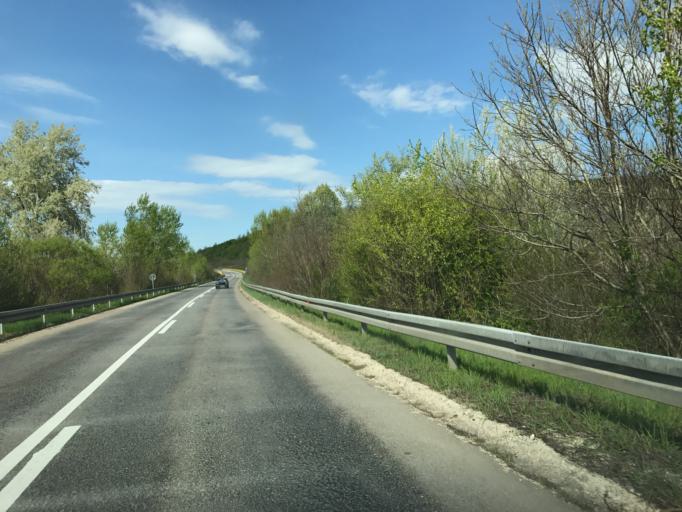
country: RS
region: Central Serbia
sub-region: Zajecarski Okrug
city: Zajecar
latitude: 43.9804
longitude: 22.2927
